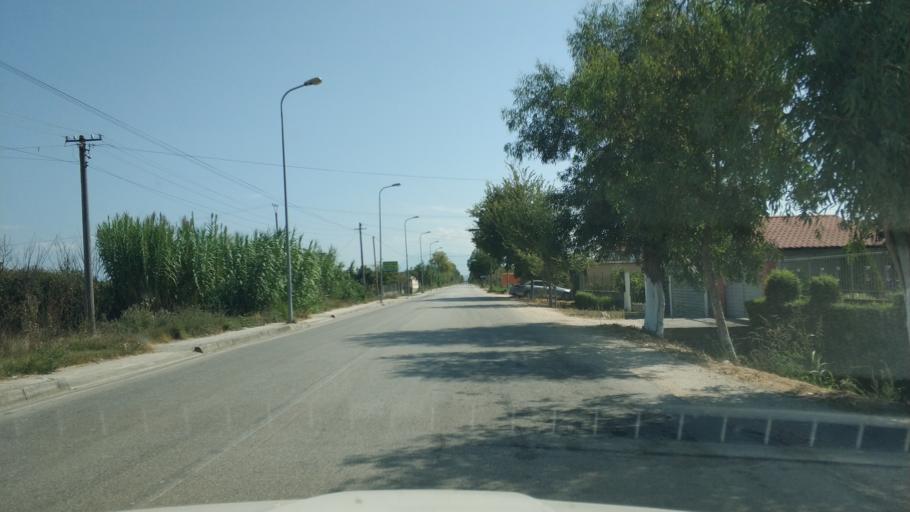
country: AL
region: Fier
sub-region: Rrethi i Lushnjes
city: Krutja e Poshtme
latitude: 40.8896
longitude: 19.6427
